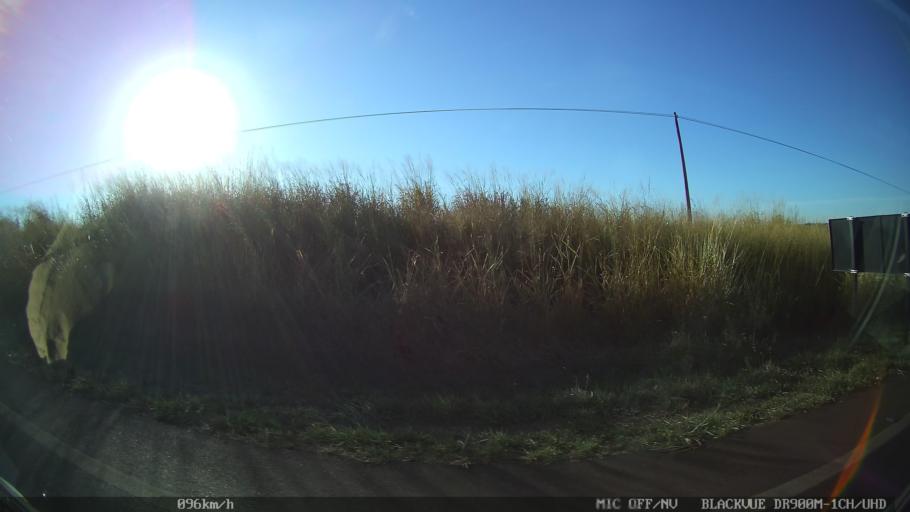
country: BR
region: Sao Paulo
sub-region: Guapiacu
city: Guapiacu
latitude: -20.7459
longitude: -49.1169
